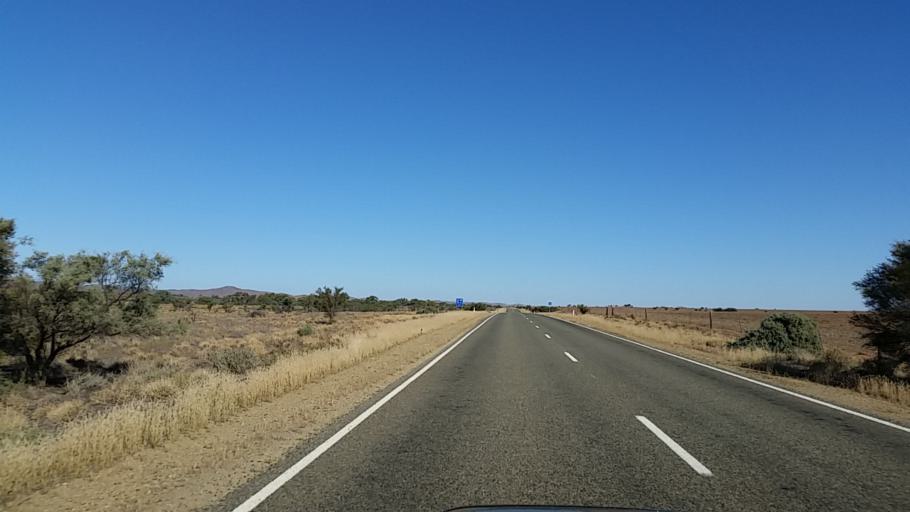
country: AU
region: South Australia
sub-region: Flinders Ranges
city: Quorn
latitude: -32.4060
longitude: 138.5176
